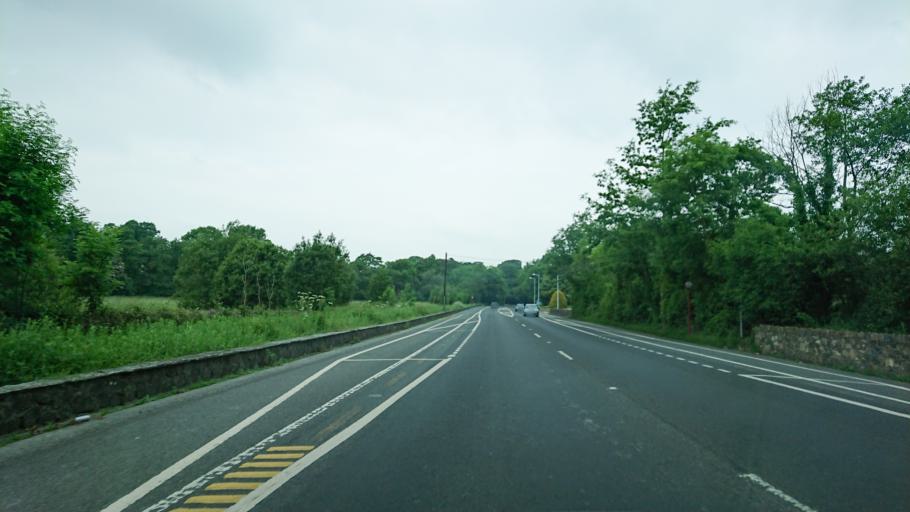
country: IE
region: Munster
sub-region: Waterford
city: Waterford
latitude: 52.2133
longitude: -7.1206
